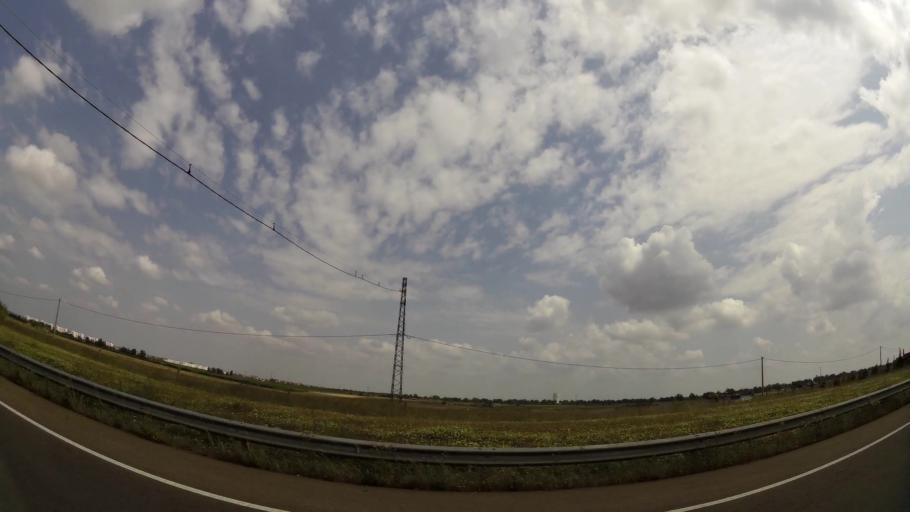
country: MA
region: Rabat-Sale-Zemmour-Zaer
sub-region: Khemisset
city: Tiflet
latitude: 33.9799
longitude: -6.5228
